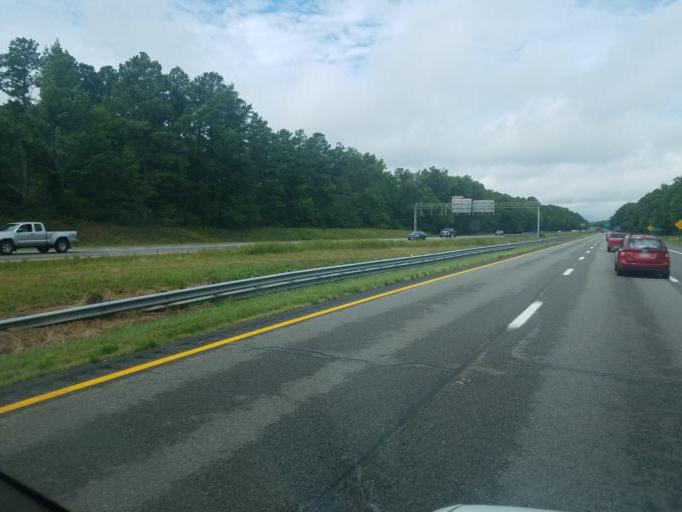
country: US
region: Virginia
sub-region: Henrico County
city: Sandston
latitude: 37.5265
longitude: -77.2931
